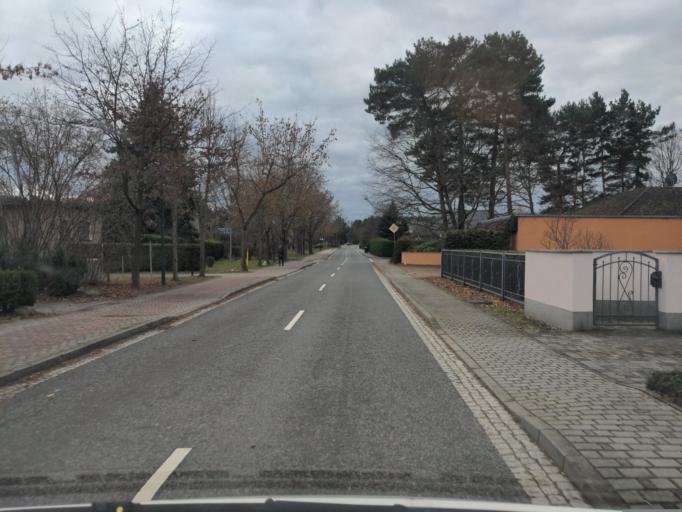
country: DE
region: Brandenburg
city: Cottbus
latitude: 51.7113
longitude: 14.3347
